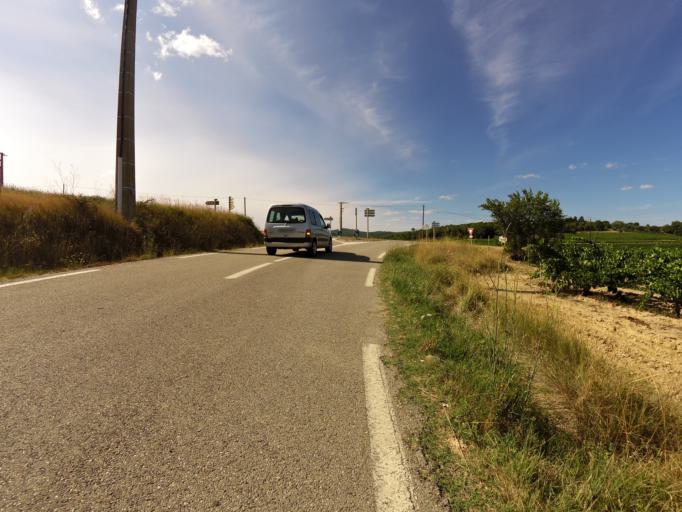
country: FR
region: Languedoc-Roussillon
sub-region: Departement du Gard
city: Lezan
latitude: 43.9834
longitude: 3.9976
